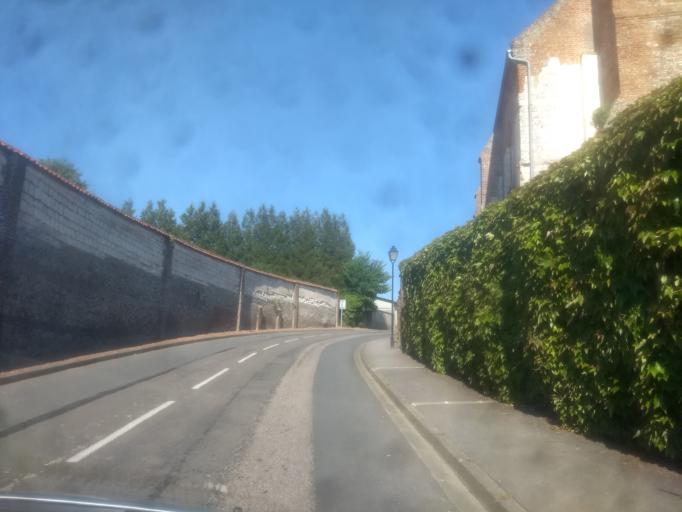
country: FR
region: Picardie
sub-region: Departement de la Somme
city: Saint-Riquier
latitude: 50.1697
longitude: 1.8804
